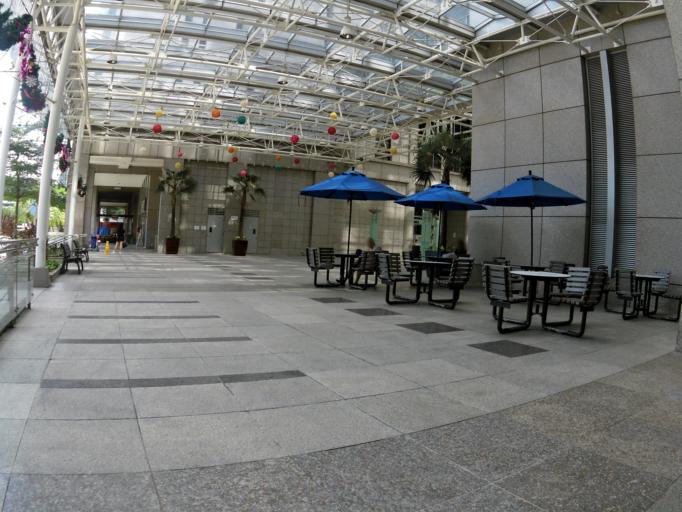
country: SG
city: Singapore
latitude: 1.2923
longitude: 103.8431
